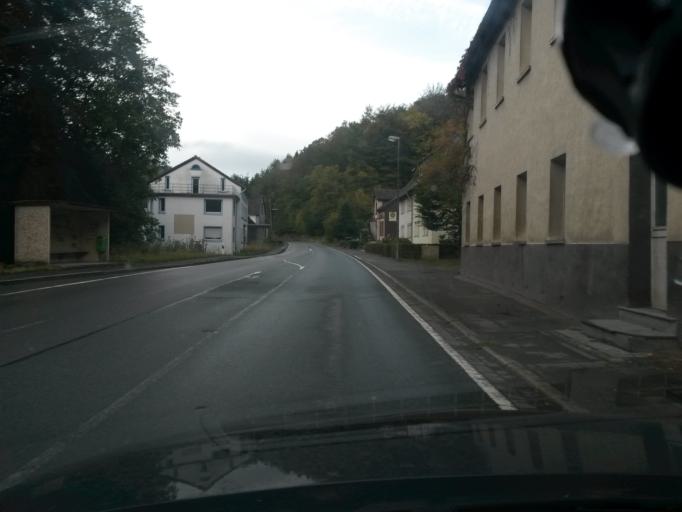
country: DE
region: North Rhine-Westphalia
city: Werdohl
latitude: 51.2394
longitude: 7.7107
